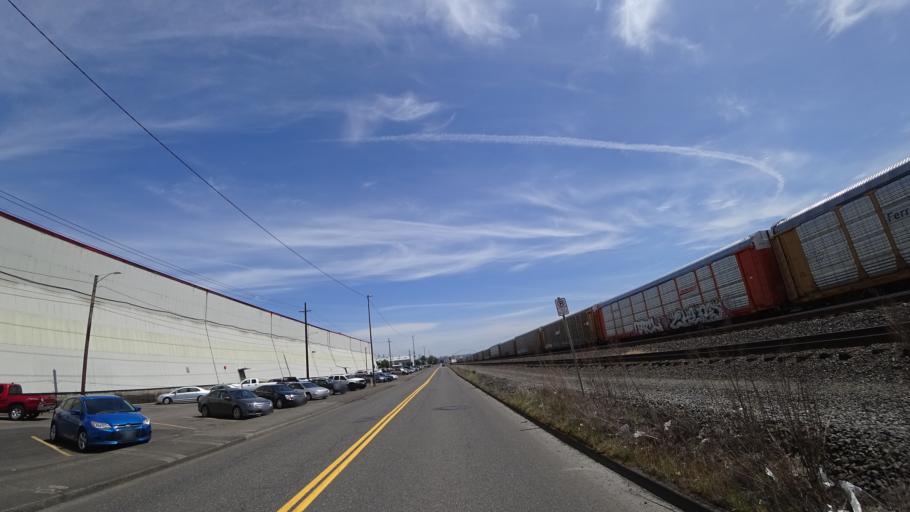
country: US
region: Oregon
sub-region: Multnomah County
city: Portland
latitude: 45.5546
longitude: -122.7224
